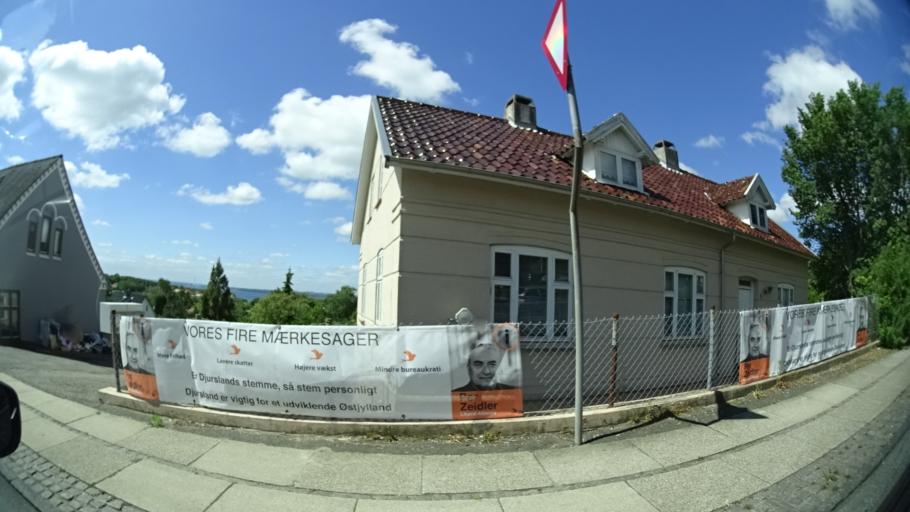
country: DK
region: Central Jutland
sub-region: Syddjurs Kommune
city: Ronde
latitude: 56.2993
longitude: 10.4821
